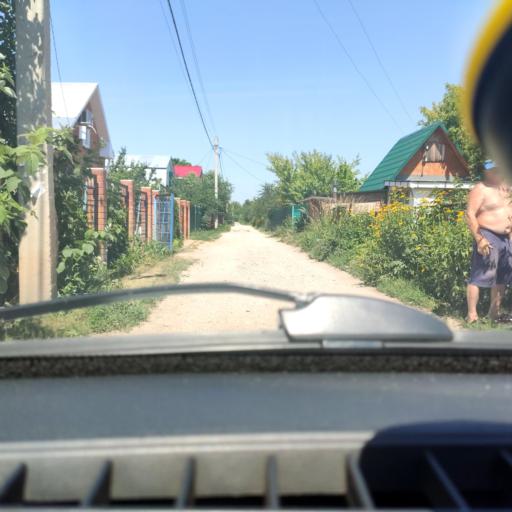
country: RU
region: Samara
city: Tol'yatti
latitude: 53.5962
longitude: 49.3049
